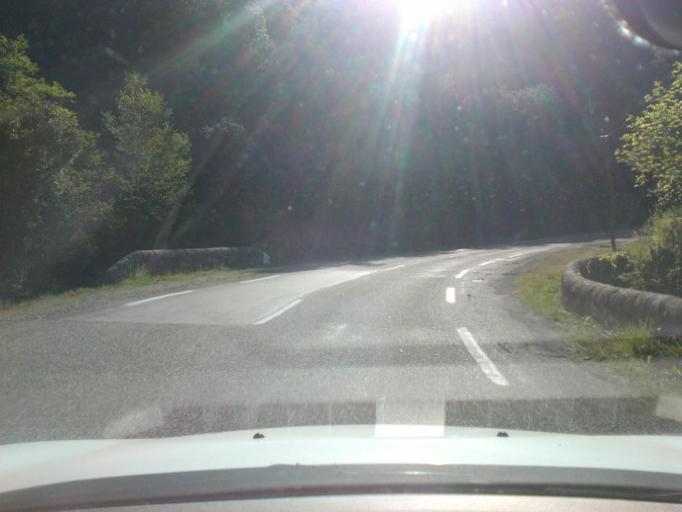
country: FR
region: Languedoc-Roussillon
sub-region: Departement du Gard
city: Lasalle
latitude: 44.1063
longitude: 3.7923
